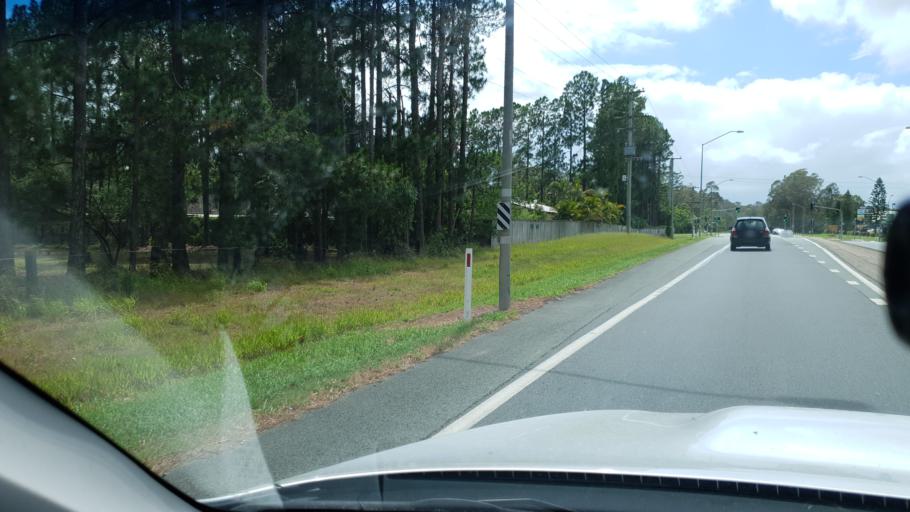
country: AU
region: Queensland
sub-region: Logan
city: Beenleigh
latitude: -27.6723
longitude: 153.2096
